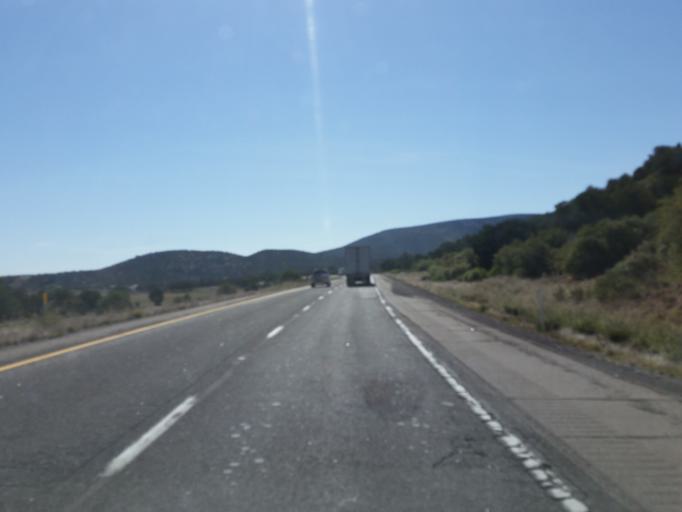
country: US
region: Arizona
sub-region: Mohave County
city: Peach Springs
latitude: 35.1810
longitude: -113.4642
